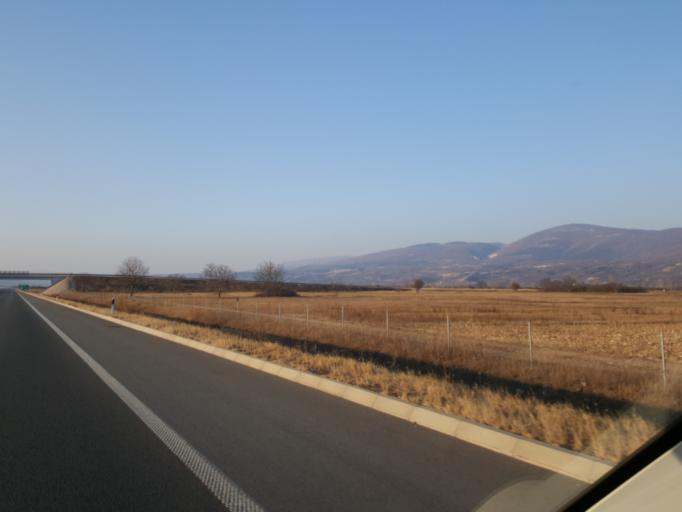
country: RS
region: Central Serbia
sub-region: Pirotski Okrug
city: Pirot
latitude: 43.1046
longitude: 22.6388
